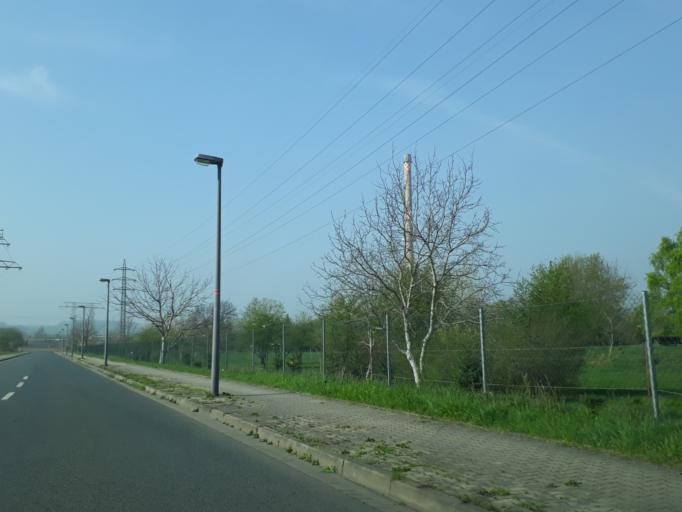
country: DE
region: Saxony
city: Heidenau
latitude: 50.9977
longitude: 13.8470
